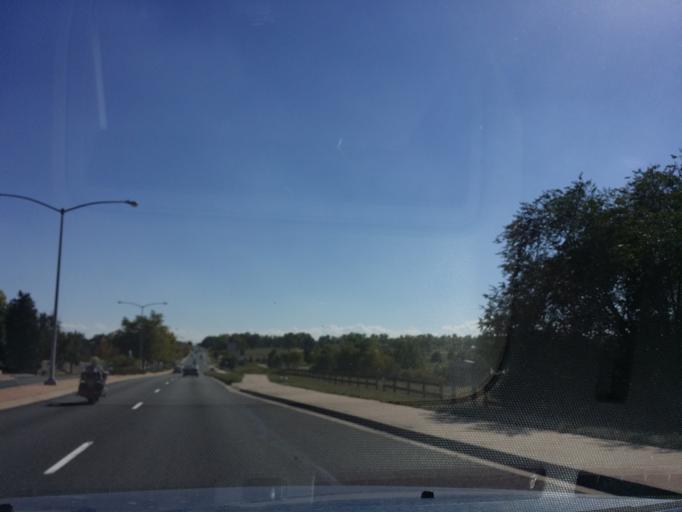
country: US
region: Colorado
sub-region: Adams County
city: Westminster
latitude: 39.8772
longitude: -105.0532
